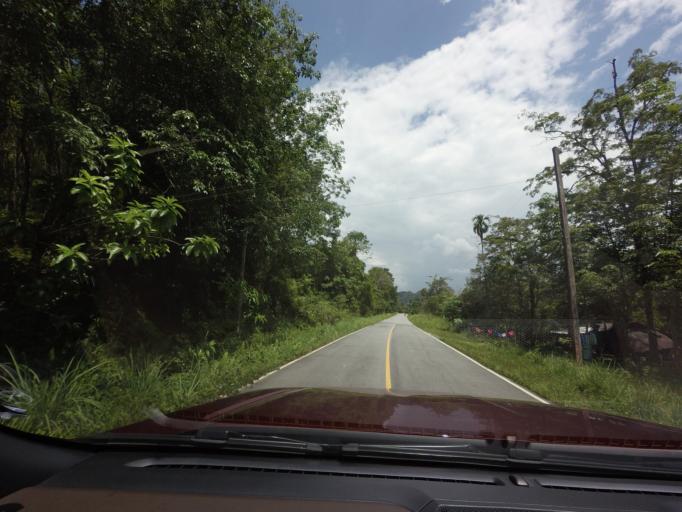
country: TH
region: Narathiwat
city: Chanae
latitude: 6.0758
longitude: 101.6874
